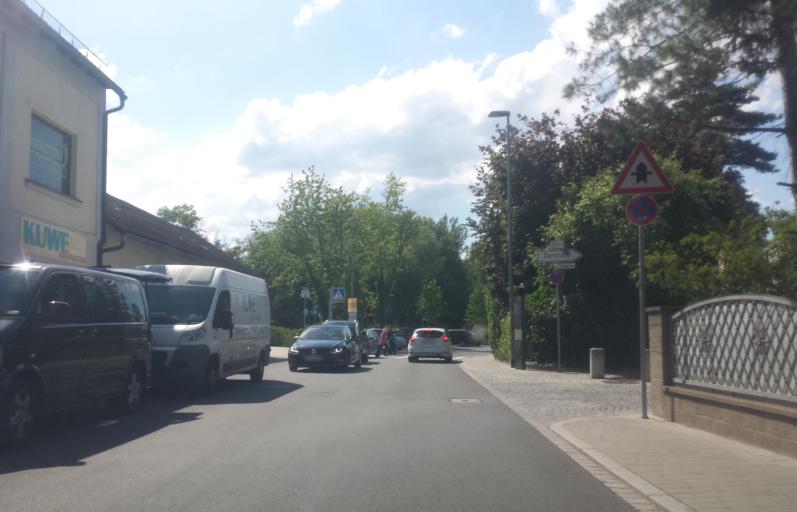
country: DE
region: Bavaria
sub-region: Regierungsbezirk Mittelfranken
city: Herzogenaurach
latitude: 49.5677
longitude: 10.8817
